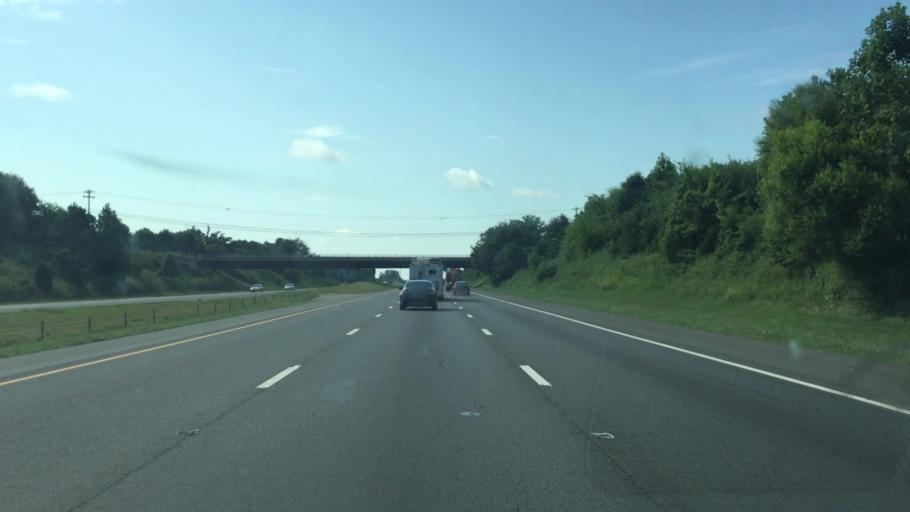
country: US
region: North Carolina
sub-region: Cabarrus County
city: Harrisburg
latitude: 35.2983
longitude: -80.6840
